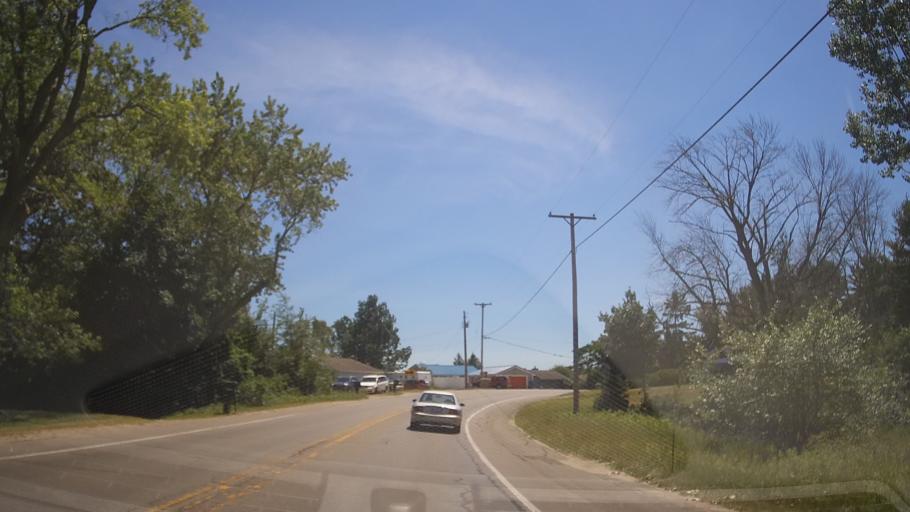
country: US
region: Michigan
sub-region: Grand Traverse County
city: Traverse City
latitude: 44.7019
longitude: -85.6912
